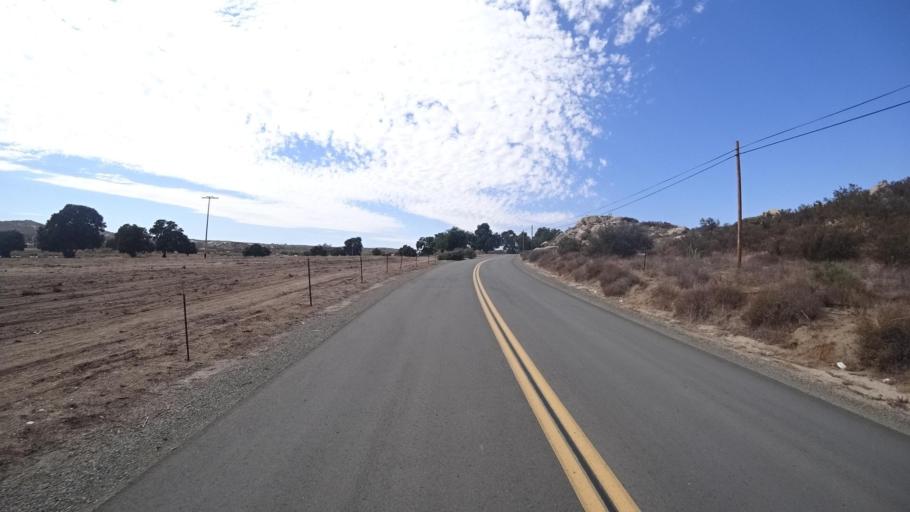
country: MX
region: Baja California
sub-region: Tecate
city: Cereso del Hongo
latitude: 32.6435
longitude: -116.2790
